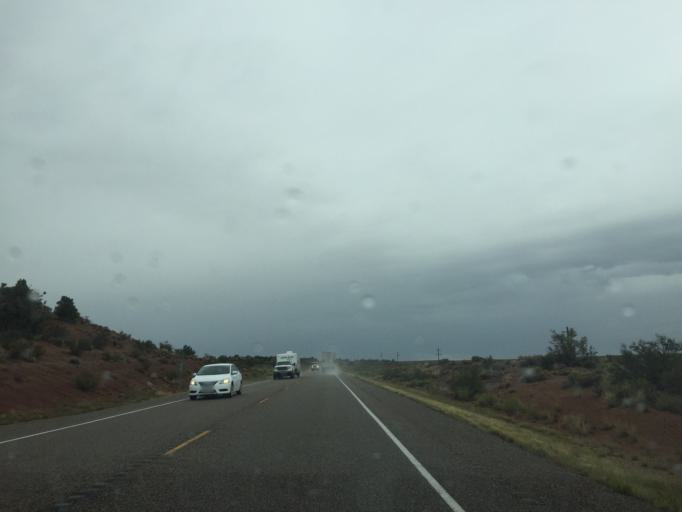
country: US
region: Utah
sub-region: Kane County
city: Kanab
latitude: 37.0640
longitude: -112.1847
